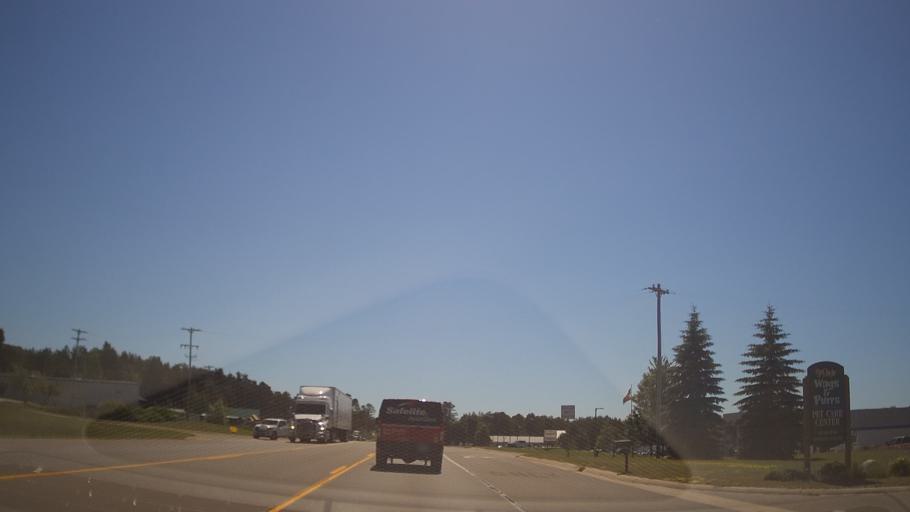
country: US
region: Michigan
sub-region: Emmet County
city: Petoskey
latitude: 45.3984
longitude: -84.8874
